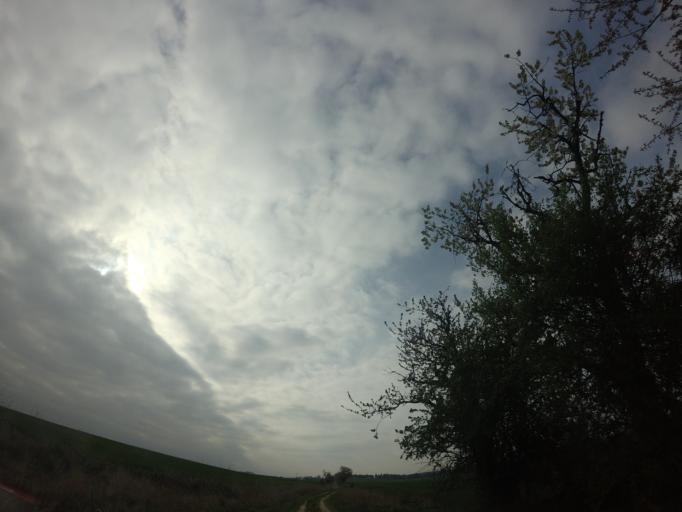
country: PL
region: West Pomeranian Voivodeship
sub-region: Powiat choszczenski
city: Pelczyce
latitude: 53.0772
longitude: 15.2364
